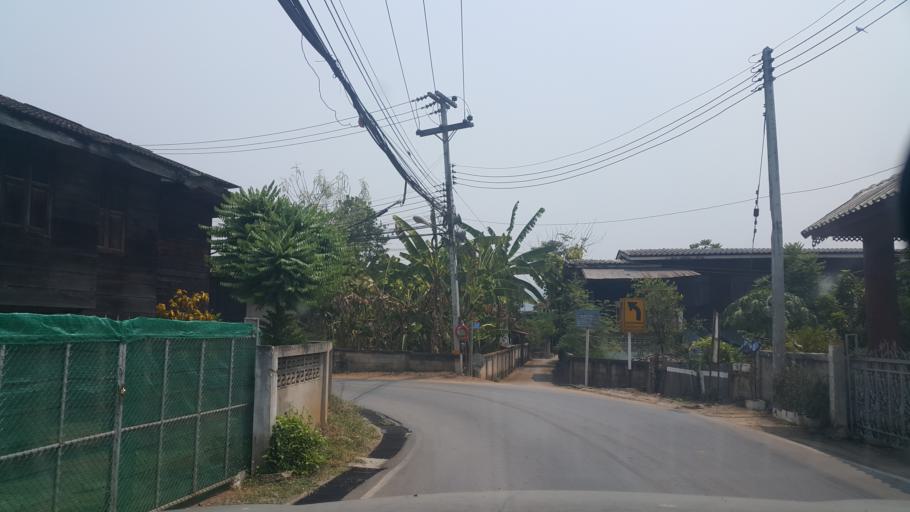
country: TH
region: Lampang
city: Soem Ngam
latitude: 18.0555
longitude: 99.2419
